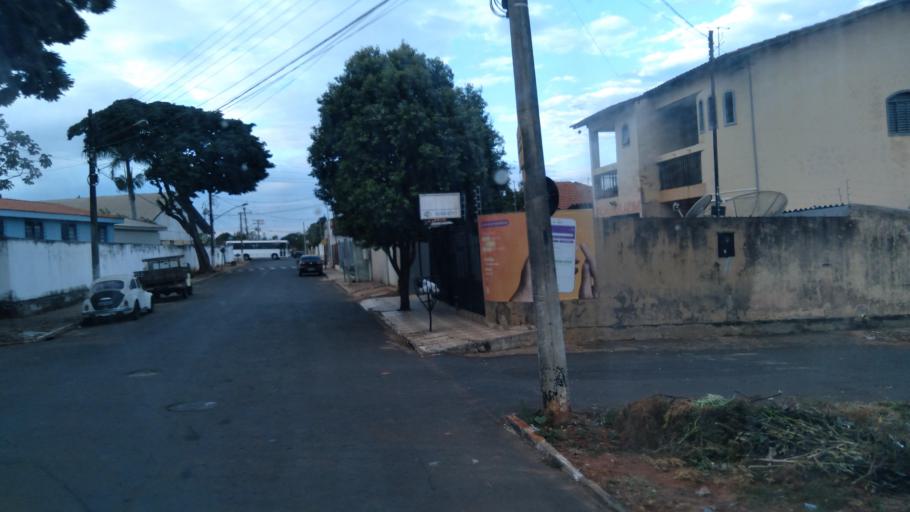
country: BR
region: Goias
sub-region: Mineiros
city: Mineiros
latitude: -17.5694
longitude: -52.5495
